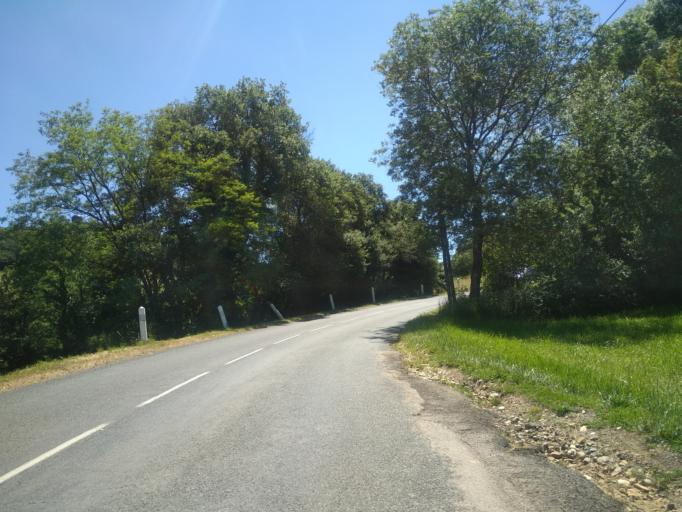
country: FR
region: Rhone-Alpes
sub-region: Departement du Rhone
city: Limonest
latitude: 45.8456
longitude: 4.7951
